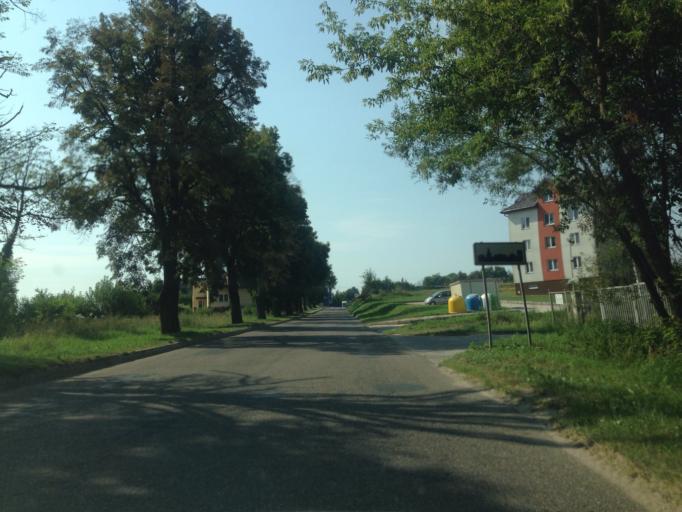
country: PL
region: Kujawsko-Pomorskie
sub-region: Powiat rypinski
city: Rypin
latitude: 53.0770
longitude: 19.4031
